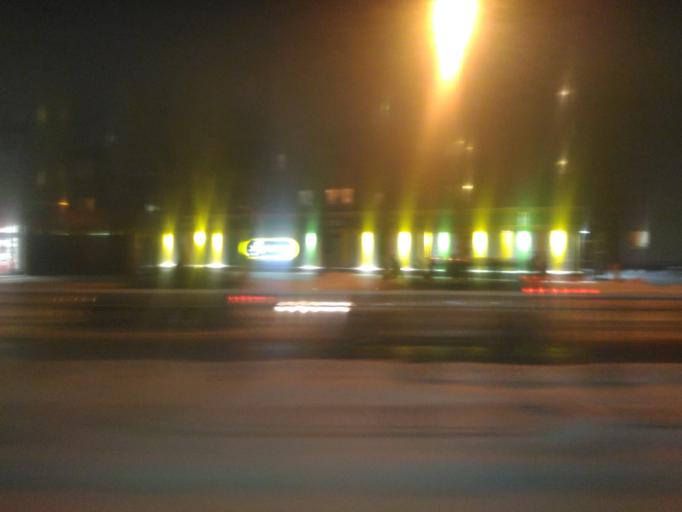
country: RU
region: Ulyanovsk
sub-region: Ulyanovskiy Rayon
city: Ulyanovsk
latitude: 54.3501
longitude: 48.3658
